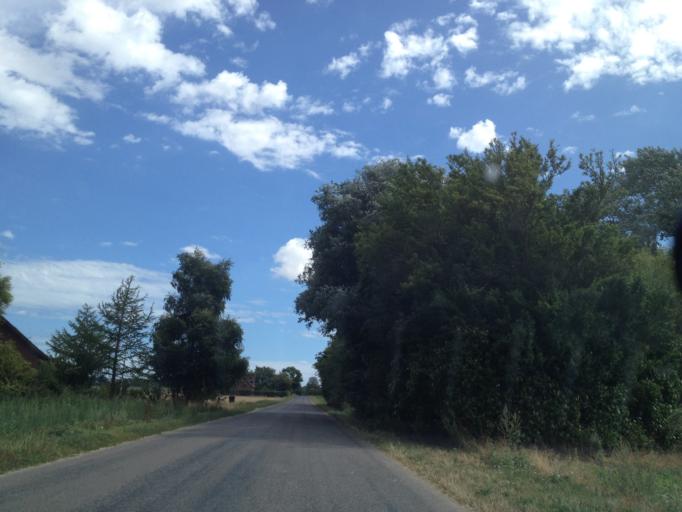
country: DK
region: Zealand
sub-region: Guldborgsund Kommune
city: Sakskobing
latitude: 54.7599
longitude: 11.6682
